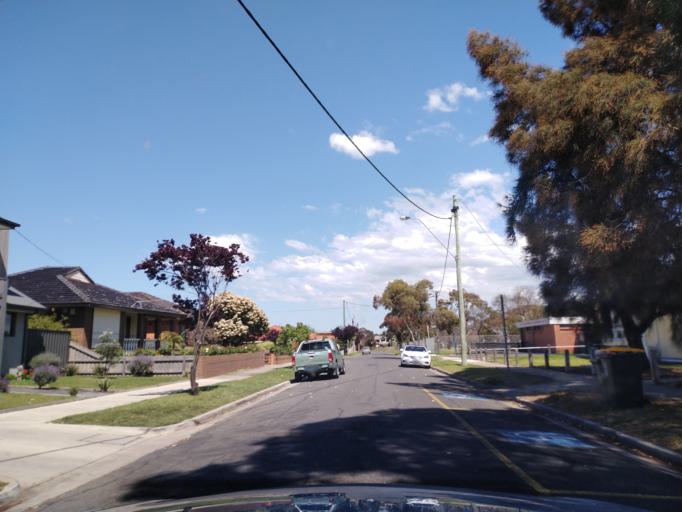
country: AU
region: Victoria
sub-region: Hobsons Bay
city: South Kingsville
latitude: -37.8355
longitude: 144.8602
